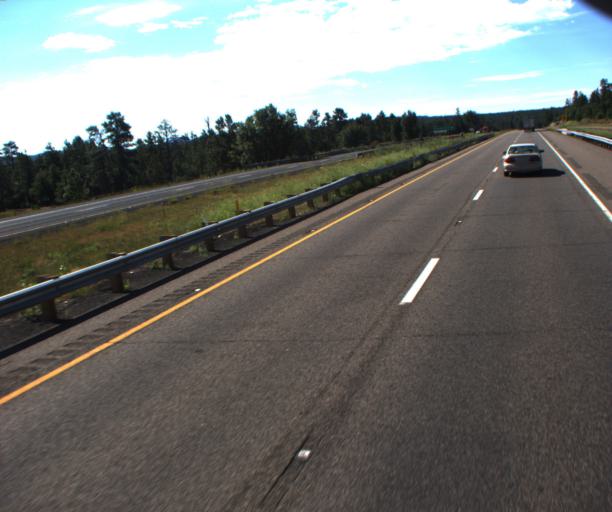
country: US
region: Arizona
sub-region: Coconino County
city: Sedona
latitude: 34.8539
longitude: -111.6077
